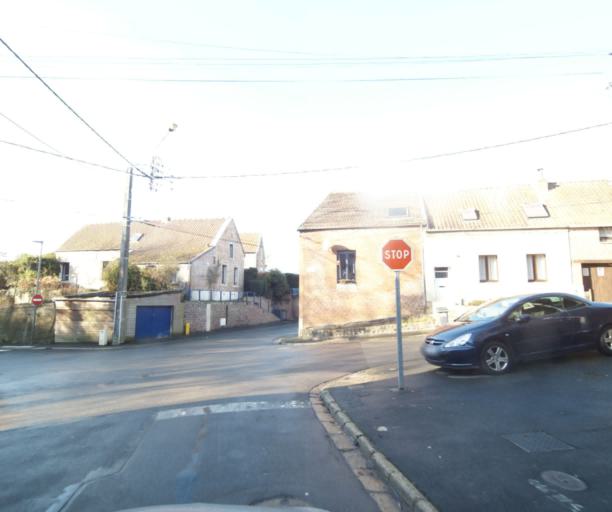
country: FR
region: Nord-Pas-de-Calais
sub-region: Departement du Nord
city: Aulnoy-lez-Valenciennes
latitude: 50.3292
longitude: 3.5347
